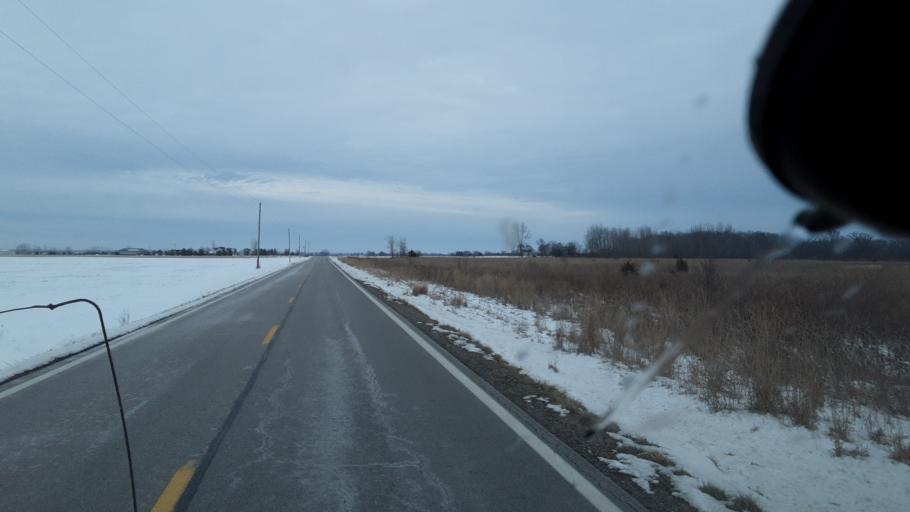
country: US
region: Ohio
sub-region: Pickaway County
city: Williamsport
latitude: 39.6334
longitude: -83.0682
